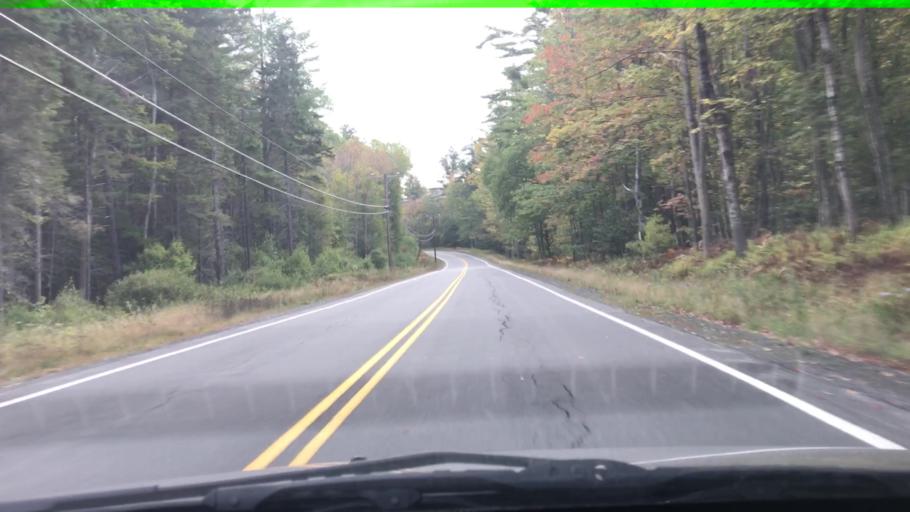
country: US
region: New Hampshire
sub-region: Sullivan County
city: Lempster
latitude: 43.0990
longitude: -72.1630
